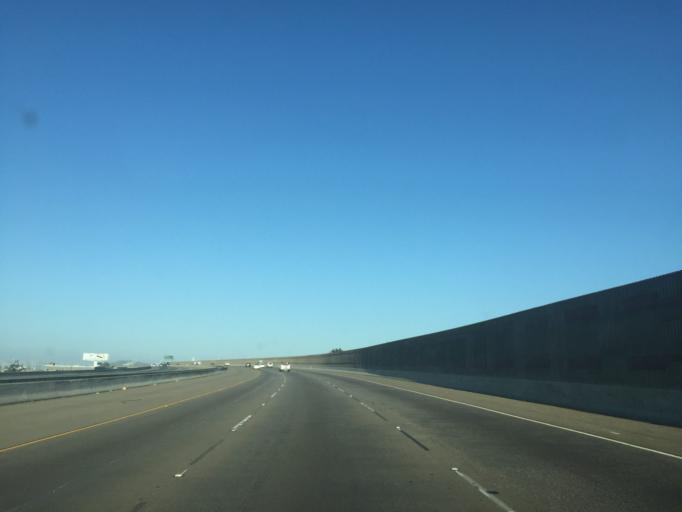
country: US
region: California
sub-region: Alameda County
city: Oakland
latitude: 37.8022
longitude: -122.2839
